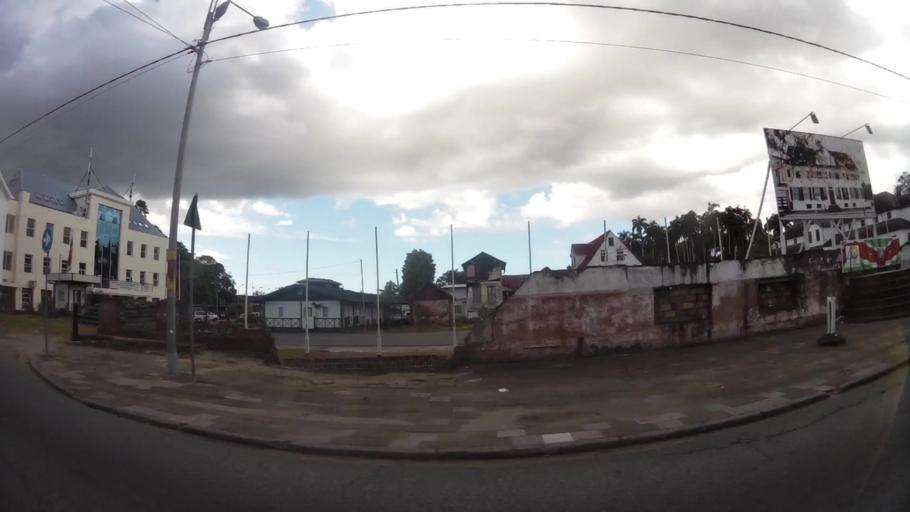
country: SR
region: Paramaribo
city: Paramaribo
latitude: 5.8272
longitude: -55.1523
